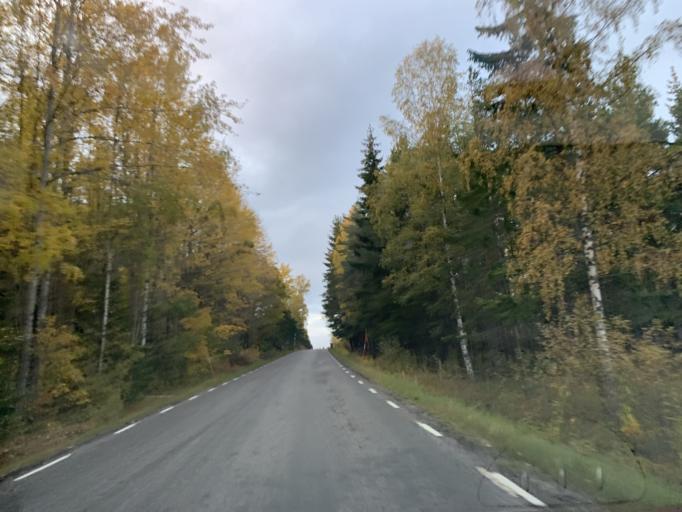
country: SE
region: Stockholm
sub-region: Nynashamns Kommun
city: Osmo
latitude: 58.9343
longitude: 17.7626
